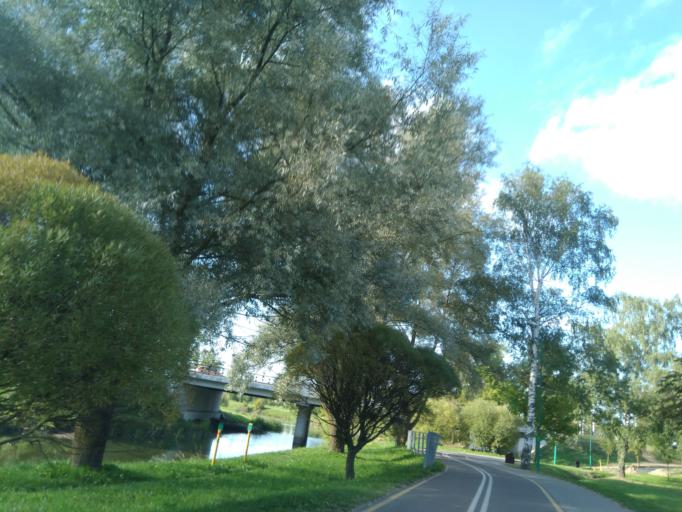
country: BY
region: Minsk
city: Minsk
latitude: 53.8733
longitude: 27.5841
